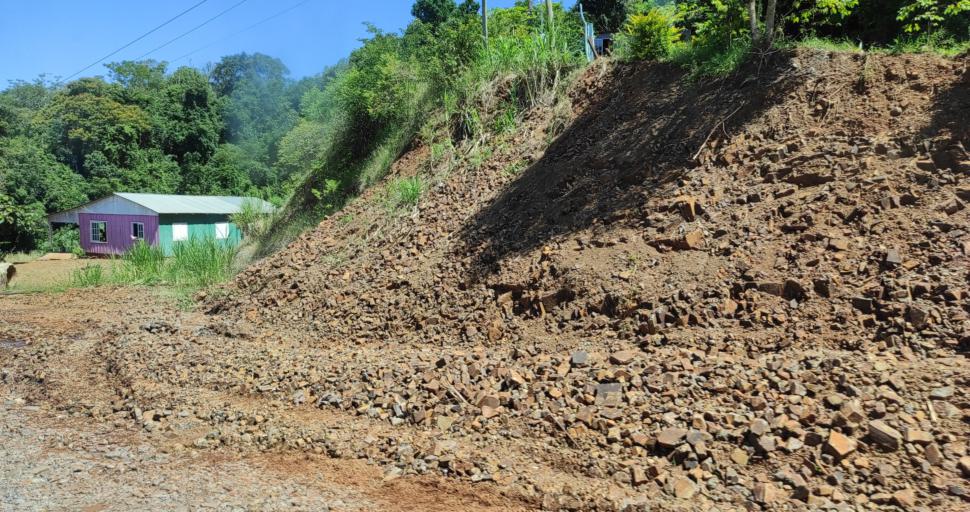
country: AR
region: Misiones
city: El Soberbio
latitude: -27.2881
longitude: -54.2146
